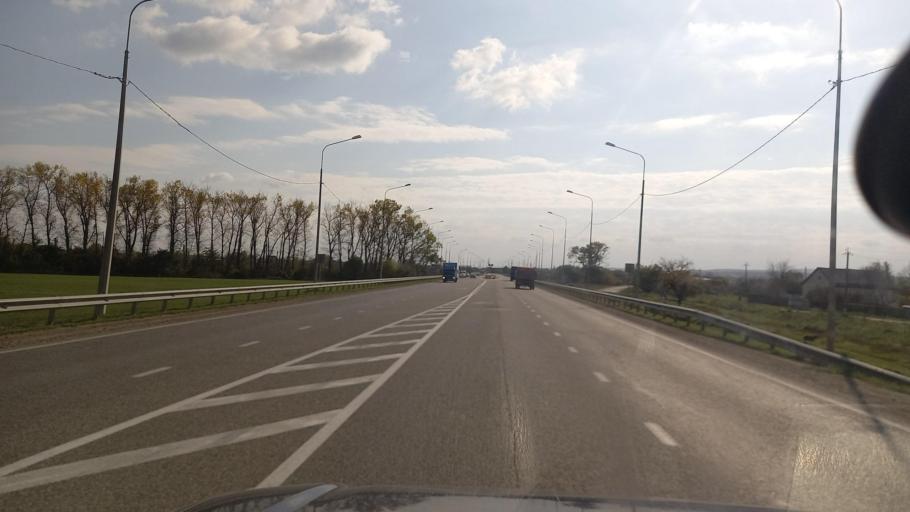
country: RU
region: Krasnodarskiy
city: Novoukrainskiy
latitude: 44.9021
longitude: 38.0352
